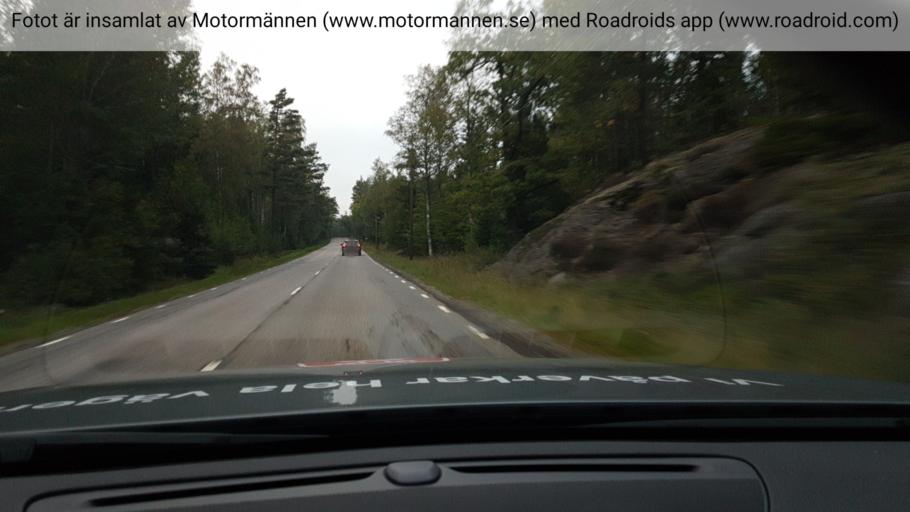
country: SE
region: Stockholm
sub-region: Haninge Kommun
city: Haninge
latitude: 59.1174
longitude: 18.1888
